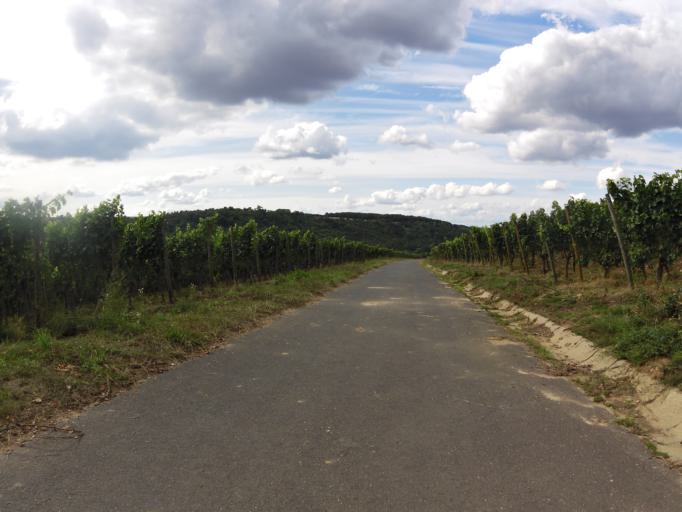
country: DE
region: Bavaria
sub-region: Regierungsbezirk Unterfranken
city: Sommerhausen
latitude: 49.6856
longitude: 10.0334
